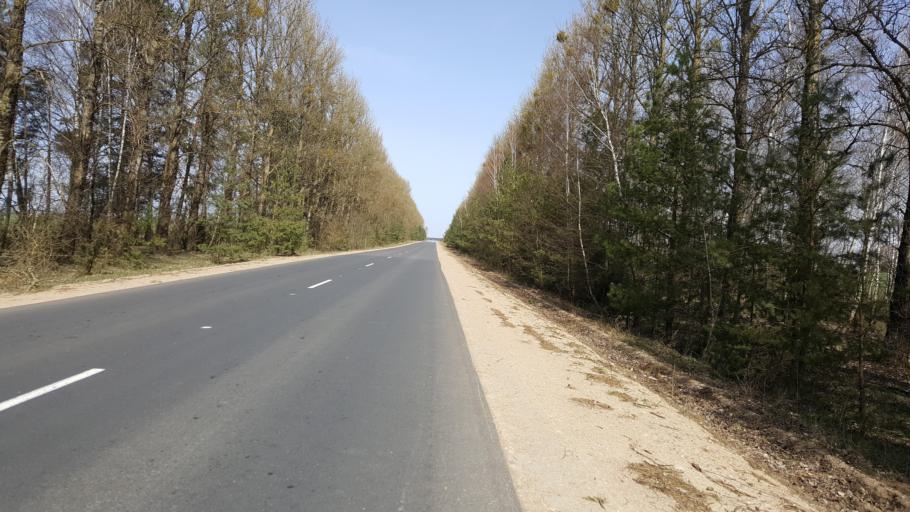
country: BY
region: Brest
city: Kamyanyets
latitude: 52.4508
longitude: 23.7371
